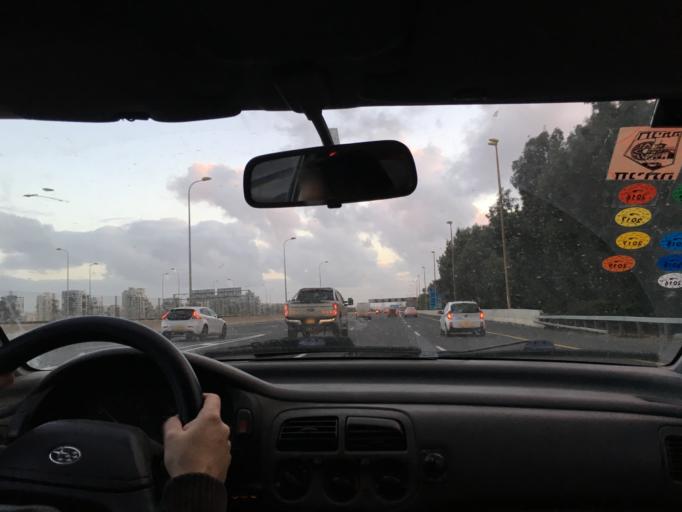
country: IL
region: Tel Aviv
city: Ramat HaSharon
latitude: 32.1343
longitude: 34.8095
